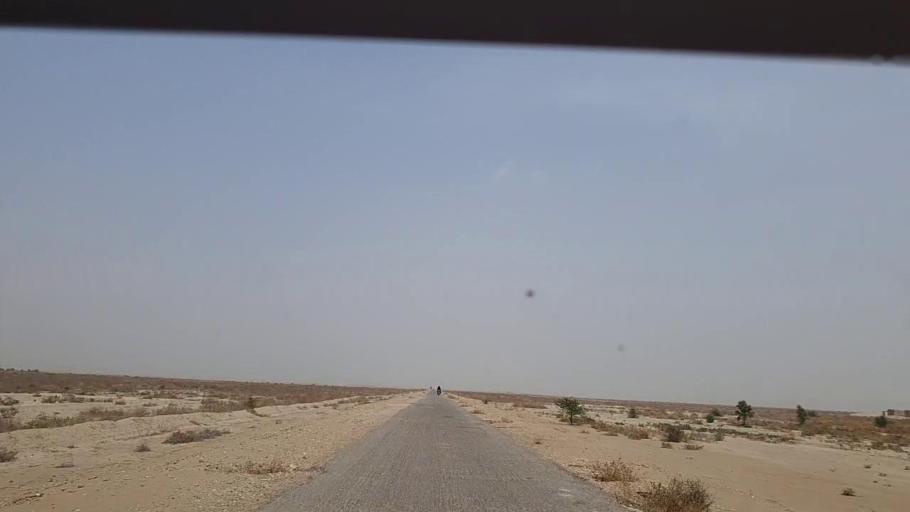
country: PK
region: Sindh
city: Phulji
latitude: 27.0009
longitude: 67.5215
